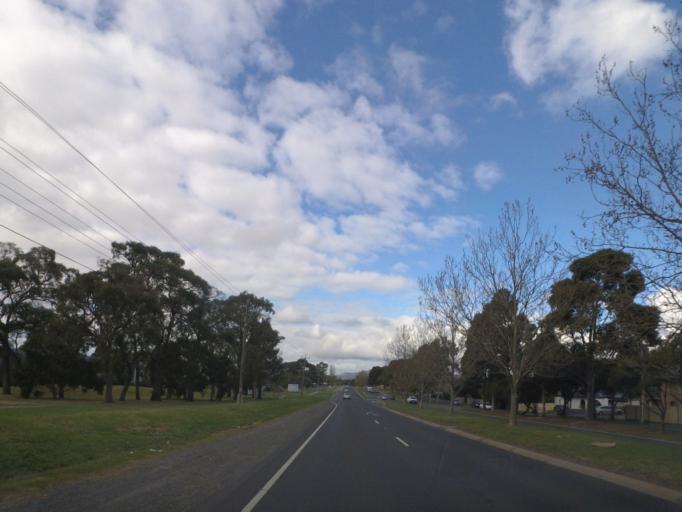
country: AU
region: Victoria
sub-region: Maroondah
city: Heathmont
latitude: -37.8445
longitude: 145.2430
